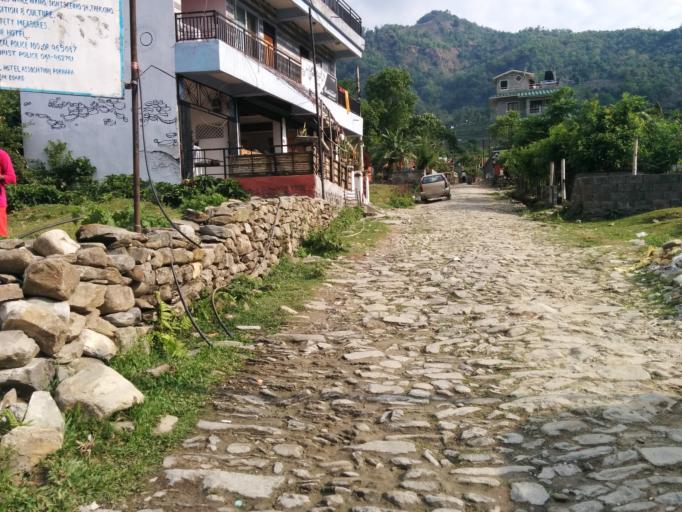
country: NP
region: Western Region
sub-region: Gandaki Zone
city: Pokhara
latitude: 28.2246
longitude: 83.9505
